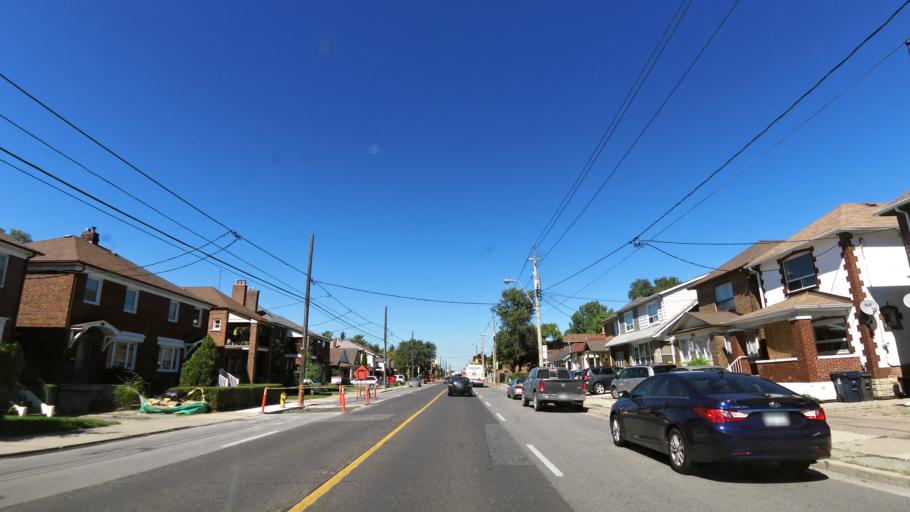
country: CA
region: Ontario
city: Etobicoke
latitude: 43.6608
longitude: -79.4892
